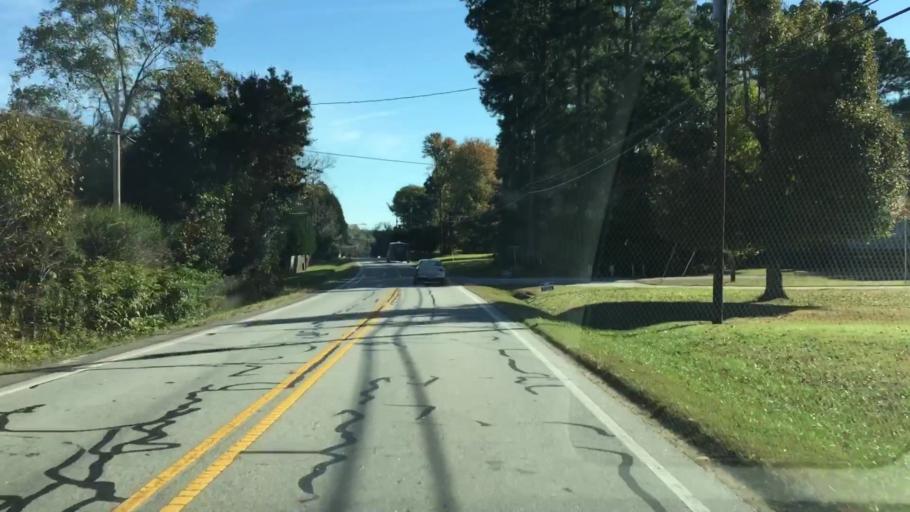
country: US
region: North Carolina
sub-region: Rowan County
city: Salisbury
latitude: 35.6612
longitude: -80.5488
